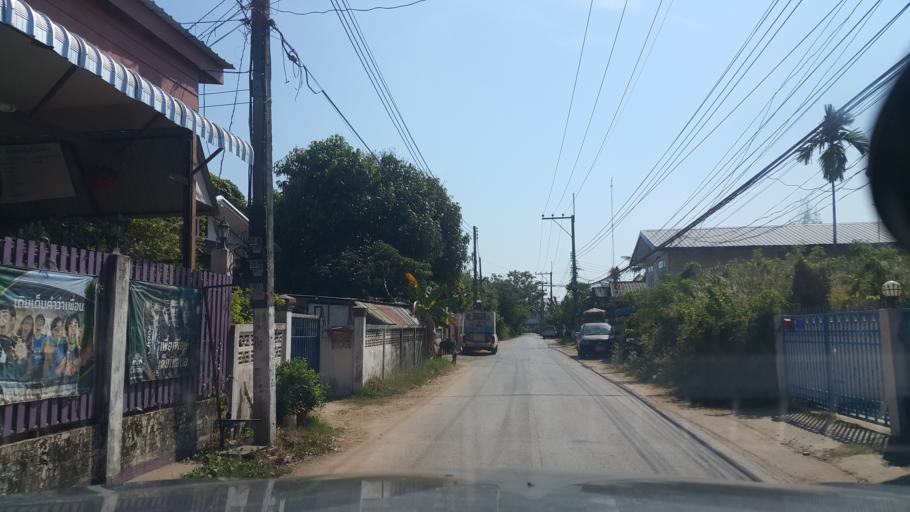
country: TH
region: Changwat Udon Thani
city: Udon Thani
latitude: 17.4569
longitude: 102.7793
